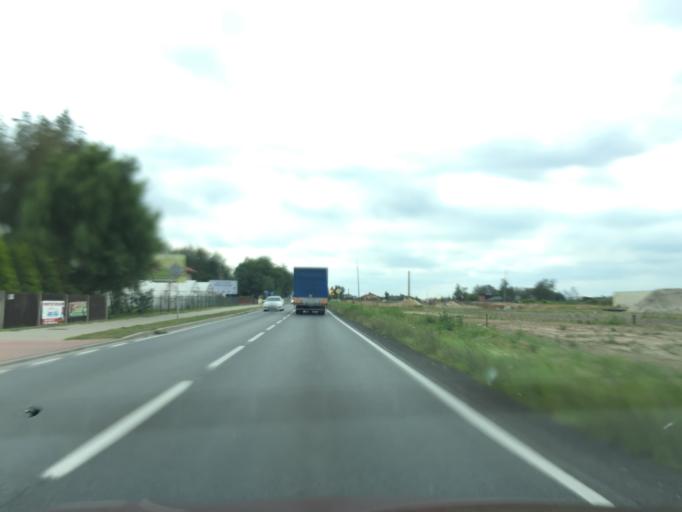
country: PL
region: Greater Poland Voivodeship
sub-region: Kalisz
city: Kalisz
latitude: 51.8077
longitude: 18.0932
